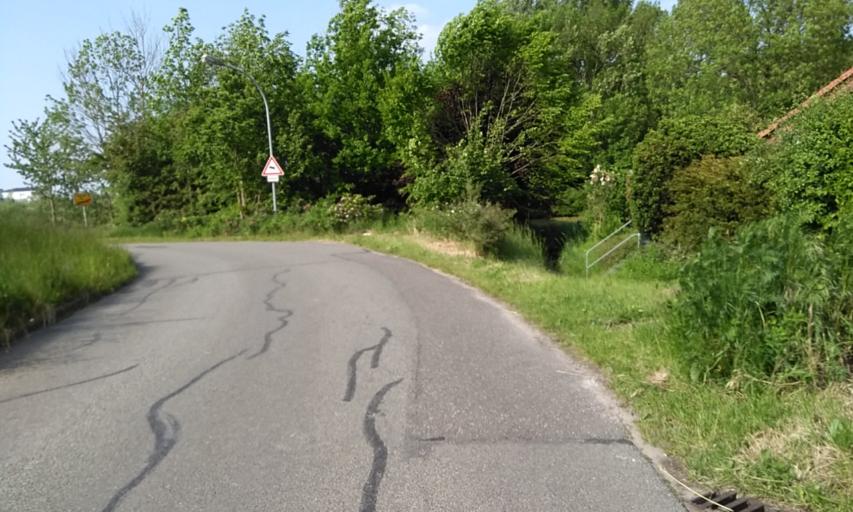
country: DE
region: Lower Saxony
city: Buxtehude
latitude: 53.4799
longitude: 9.7053
